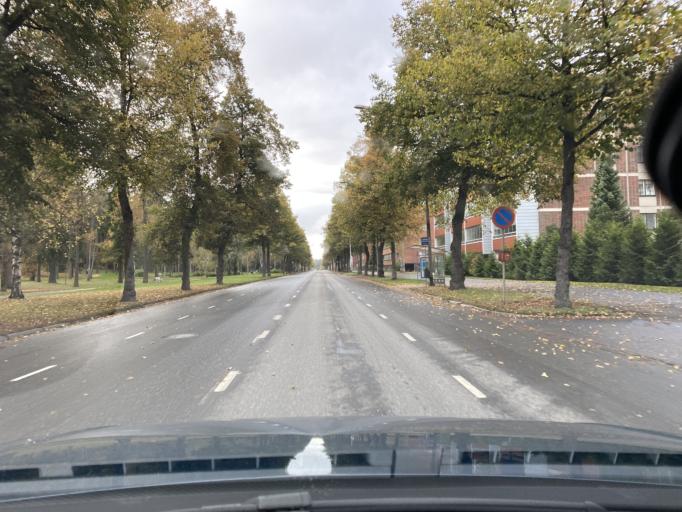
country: FI
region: Haeme
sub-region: Forssa
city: Forssa
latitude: 60.8171
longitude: 23.6125
